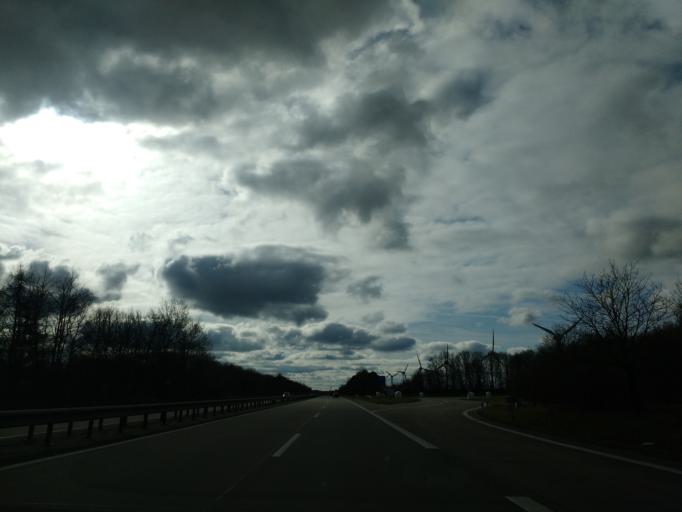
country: DE
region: Lower Saxony
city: Midlum
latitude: 53.7279
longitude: 8.6618
